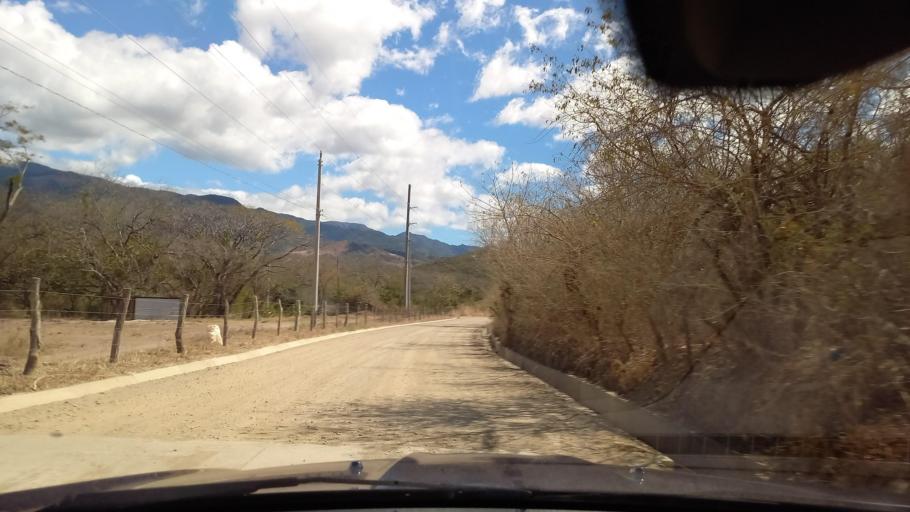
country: SV
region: Santa Ana
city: Metapan
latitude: 14.3600
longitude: -89.4692
